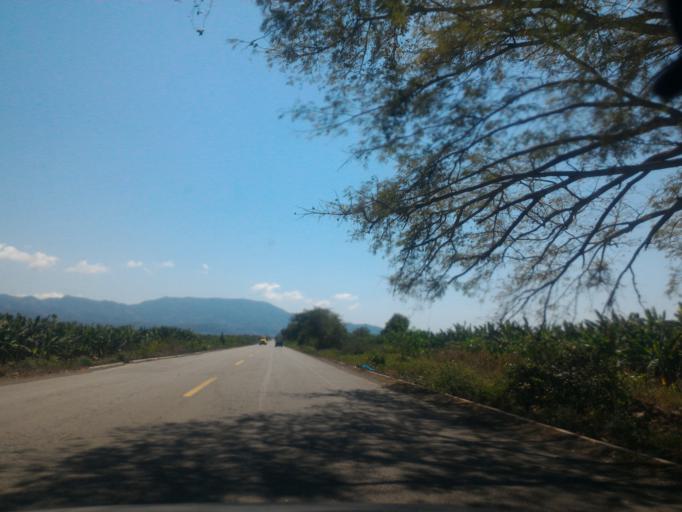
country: MX
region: Michoacan
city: Coahuayana Viejo
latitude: 18.7002
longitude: -103.7043
